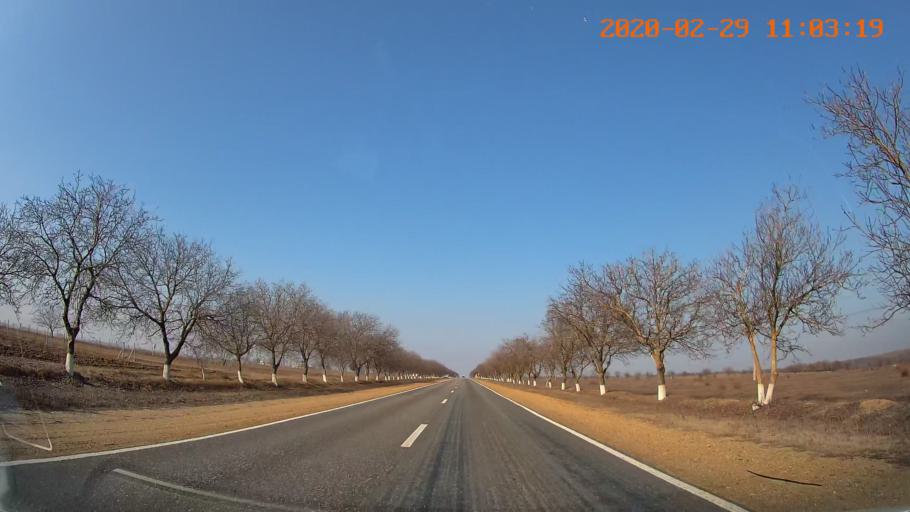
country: MD
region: Criuleni
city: Criuleni
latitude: 47.1788
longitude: 29.2199
